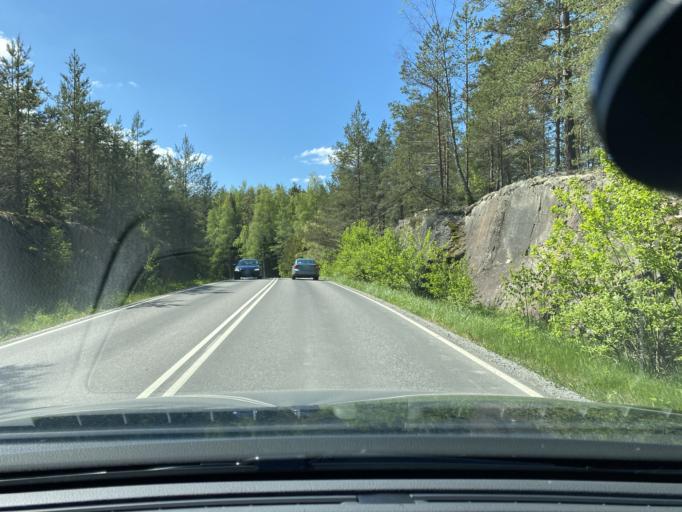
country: FI
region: Varsinais-Suomi
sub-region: Salo
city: Halikko
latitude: 60.3359
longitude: 22.9430
